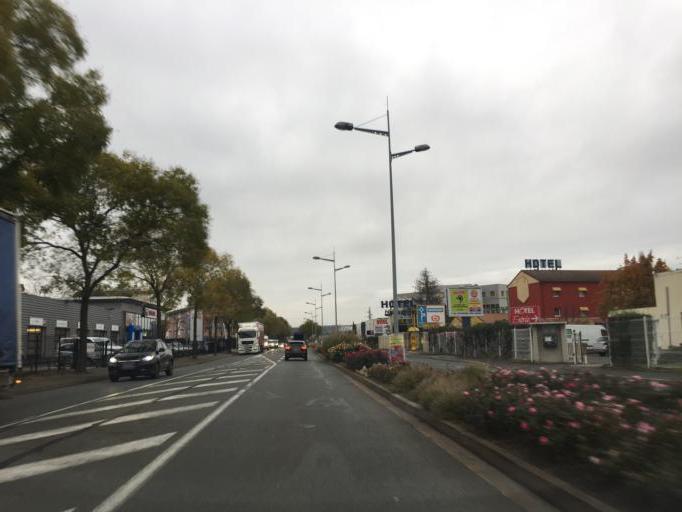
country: FR
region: Rhone-Alpes
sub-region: Departement de l'Ain
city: Jassans-Riottier
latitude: 45.9806
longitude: 4.7401
